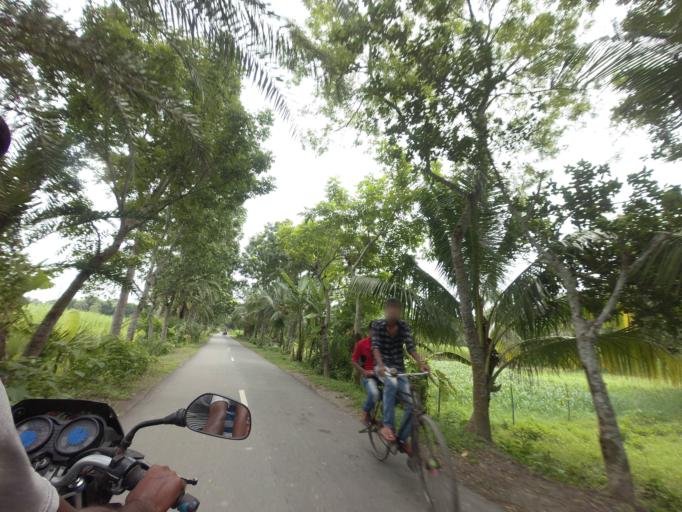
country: BD
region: Khulna
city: Kalia
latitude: 23.1059
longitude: 89.6471
